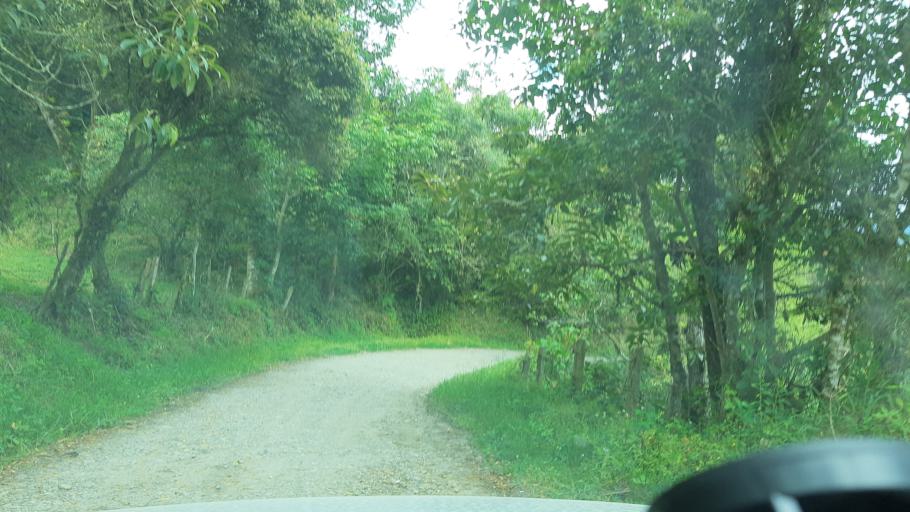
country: CO
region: Boyaca
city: Garagoa
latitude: 5.0482
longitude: -73.3505
